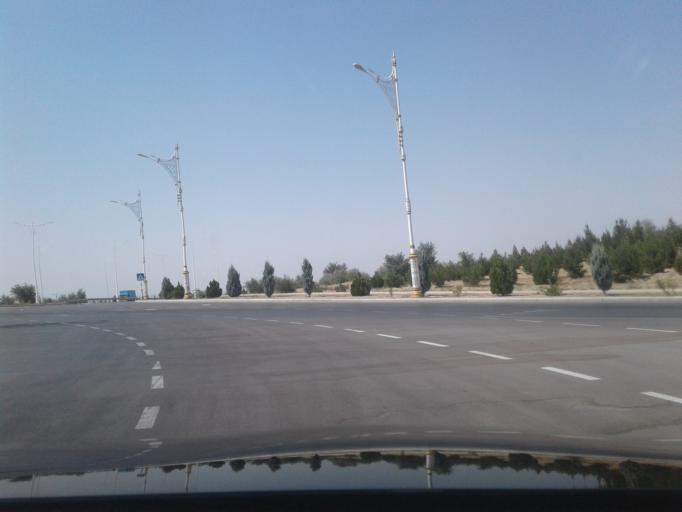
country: TM
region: Ahal
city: Ashgabat
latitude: 37.8781
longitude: 58.4229
